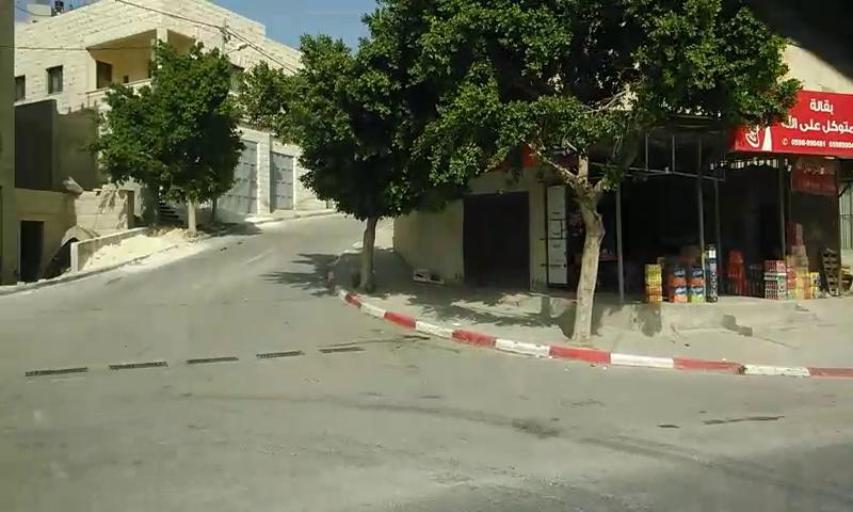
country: PS
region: West Bank
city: Dayr Sharaf
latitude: 32.2514
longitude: 35.1878
